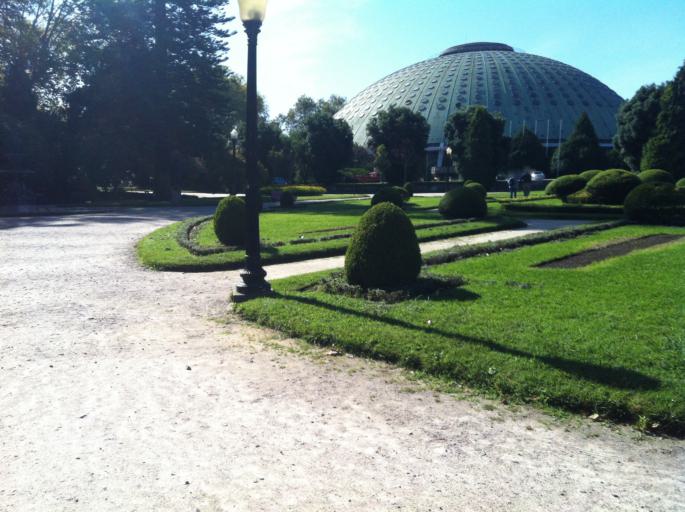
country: PT
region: Porto
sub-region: Porto
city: Porto
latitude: 41.1482
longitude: -8.6254
